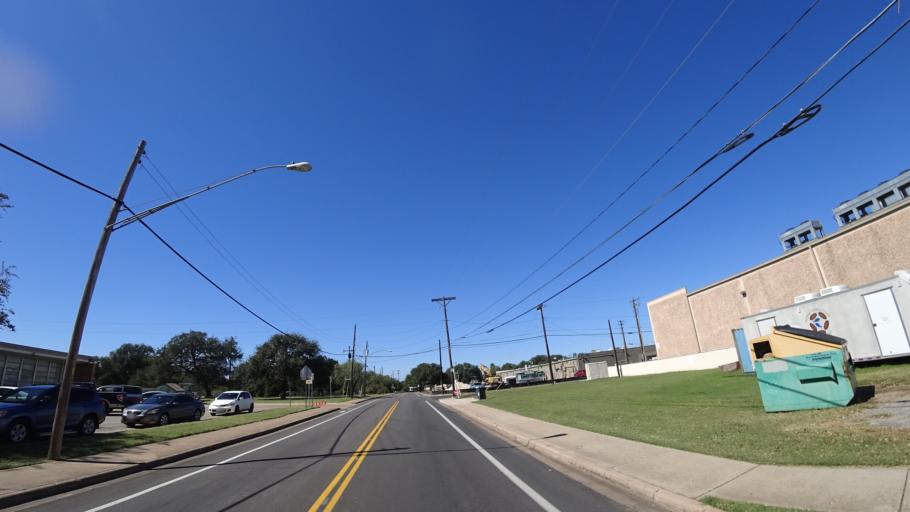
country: US
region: Texas
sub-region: Travis County
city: Rollingwood
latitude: 30.2287
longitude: -97.7903
